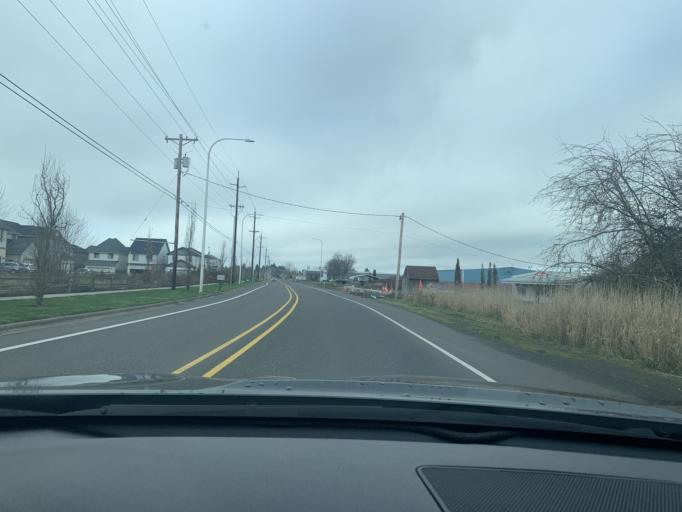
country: US
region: Oregon
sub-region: Washington County
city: North Plains
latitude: 45.5963
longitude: -122.9723
